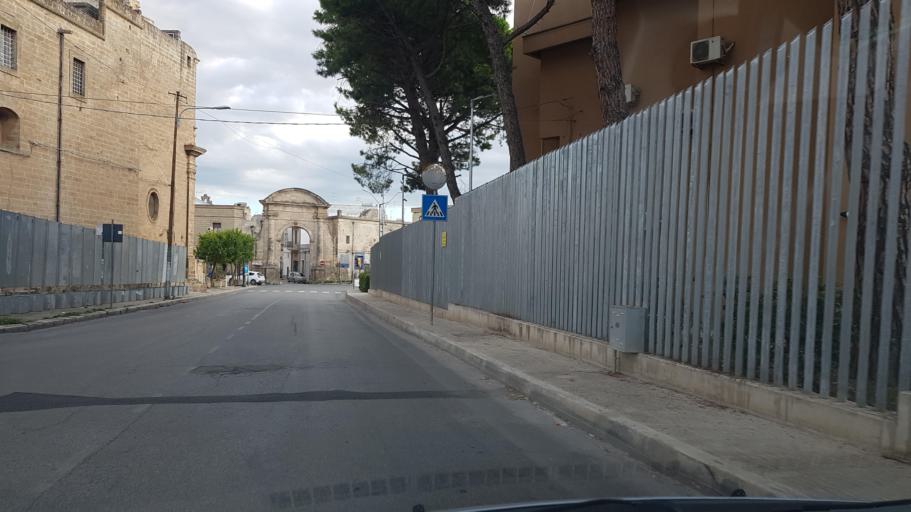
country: IT
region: Apulia
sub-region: Provincia di Brindisi
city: Francavilla Fontana
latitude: 40.5347
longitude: 17.5785
